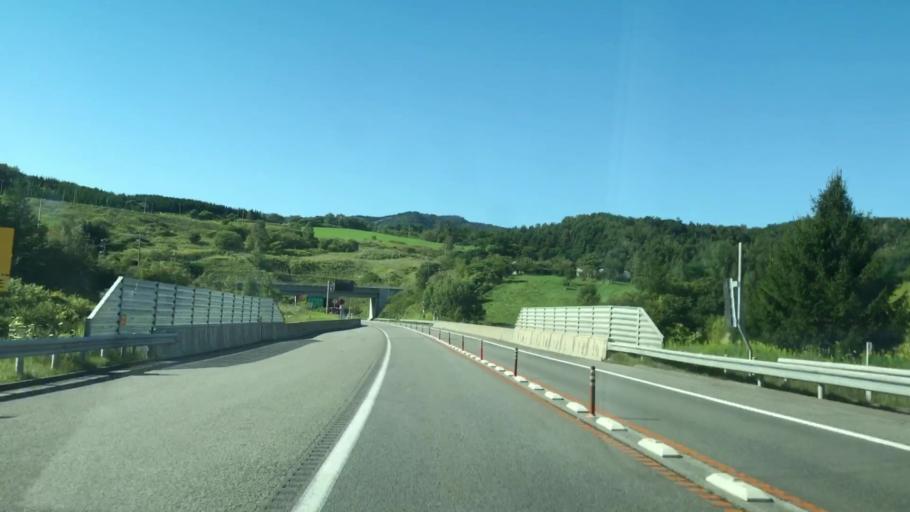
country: JP
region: Hokkaido
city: Date
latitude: 42.5501
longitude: 140.7903
